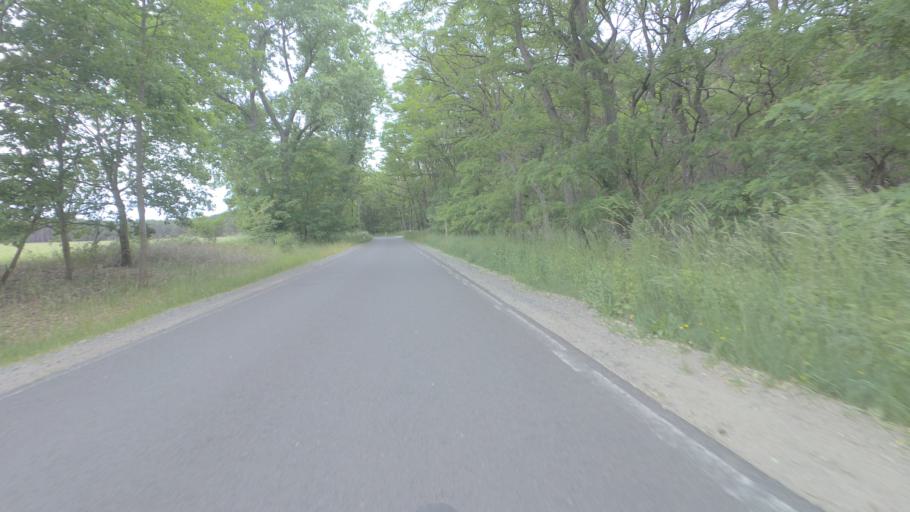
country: DE
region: Brandenburg
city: Bestensee
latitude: 52.2486
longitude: 13.7683
